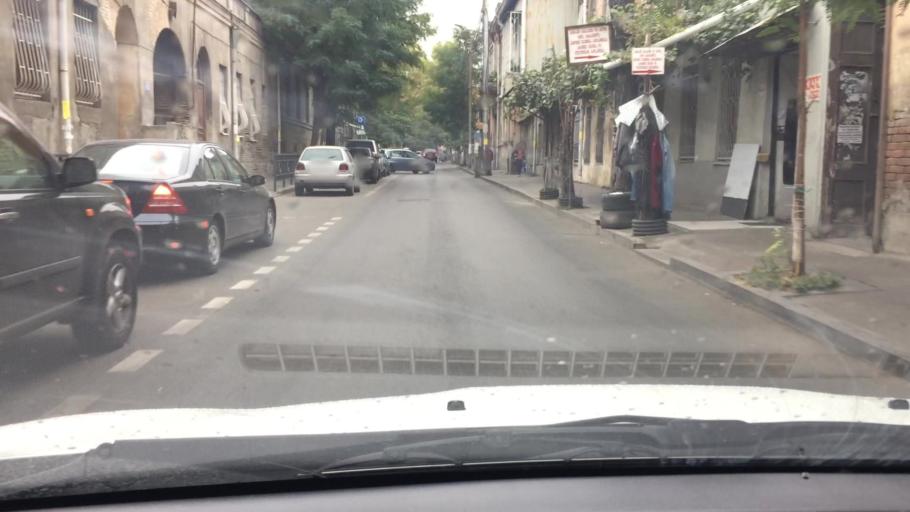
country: GE
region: T'bilisi
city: Tbilisi
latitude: 41.7113
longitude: 44.8018
